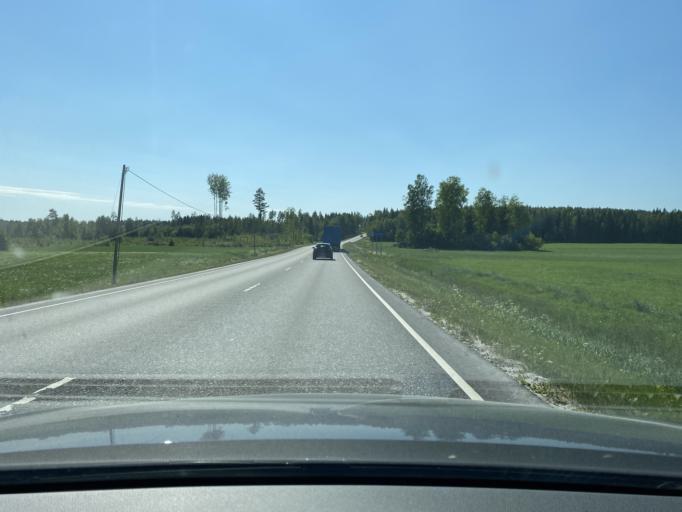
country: FI
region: Pirkanmaa
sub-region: Lounais-Pirkanmaa
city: Mouhijaervi
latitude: 61.3915
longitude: 23.2230
